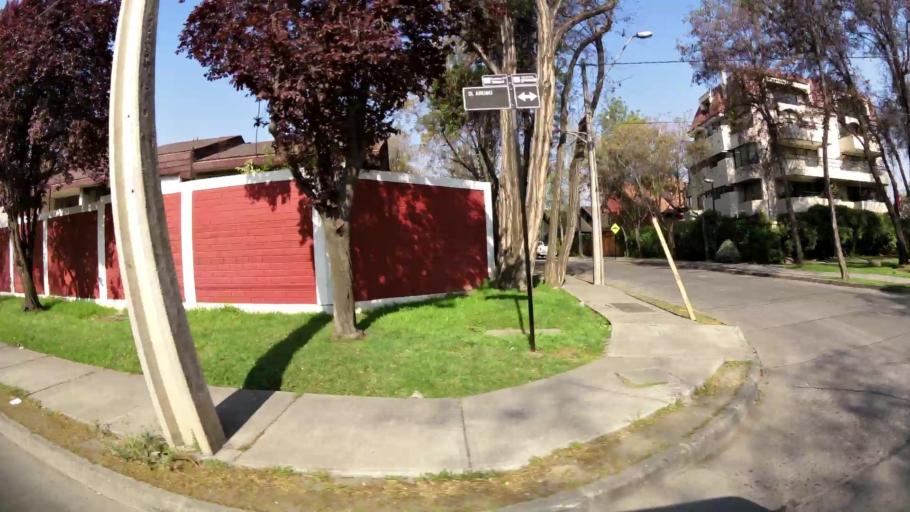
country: CL
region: Santiago Metropolitan
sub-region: Provincia de Santiago
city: Villa Presidente Frei, Nunoa, Santiago, Chile
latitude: -33.3792
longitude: -70.5575
